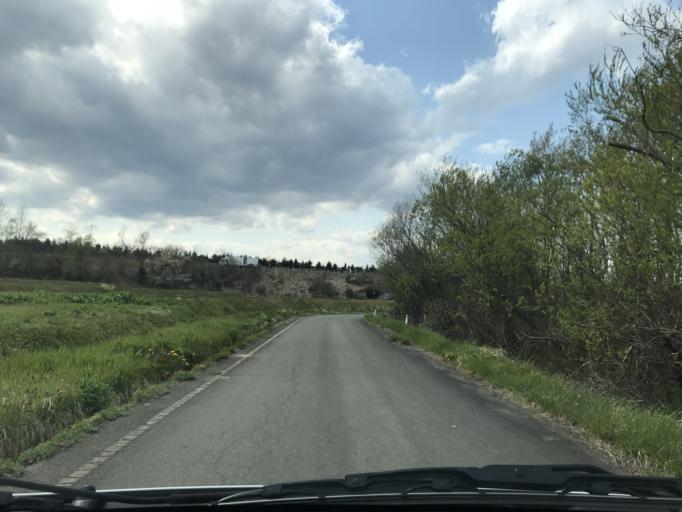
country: JP
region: Iwate
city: Mizusawa
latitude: 39.0719
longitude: 141.1022
